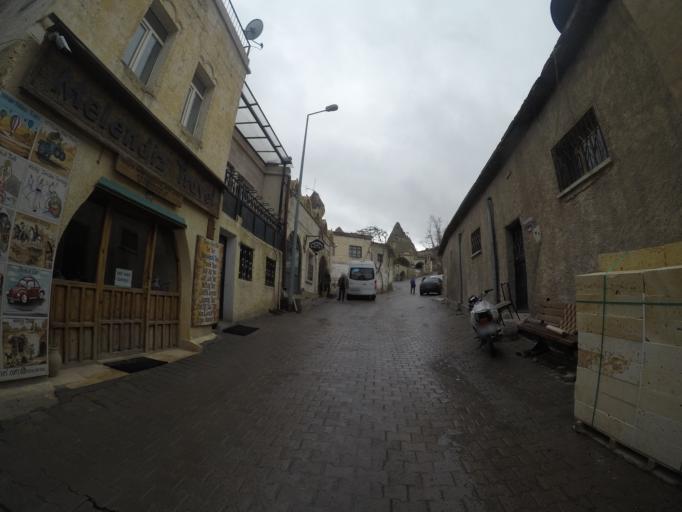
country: TR
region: Nevsehir
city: Goereme
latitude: 38.6420
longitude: 34.8300
